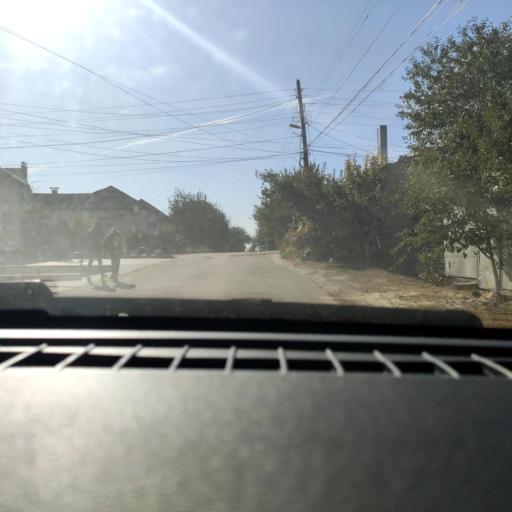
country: RU
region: Voronezj
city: Voronezh
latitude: 51.6714
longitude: 39.2667
